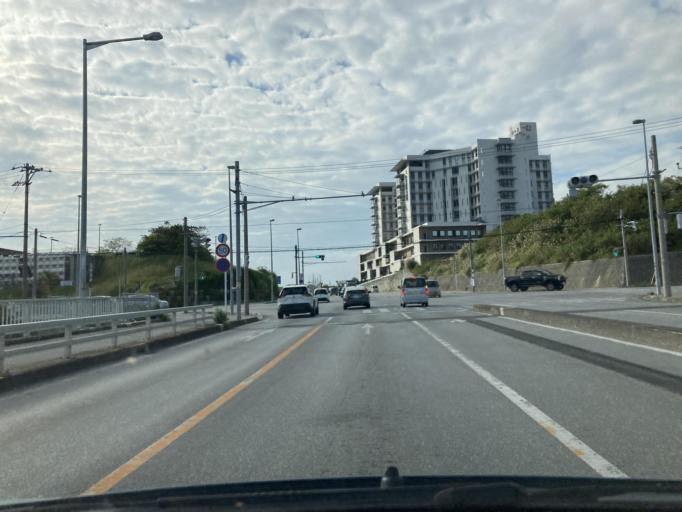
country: JP
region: Okinawa
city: Okinawa
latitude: 26.3162
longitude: 127.7996
